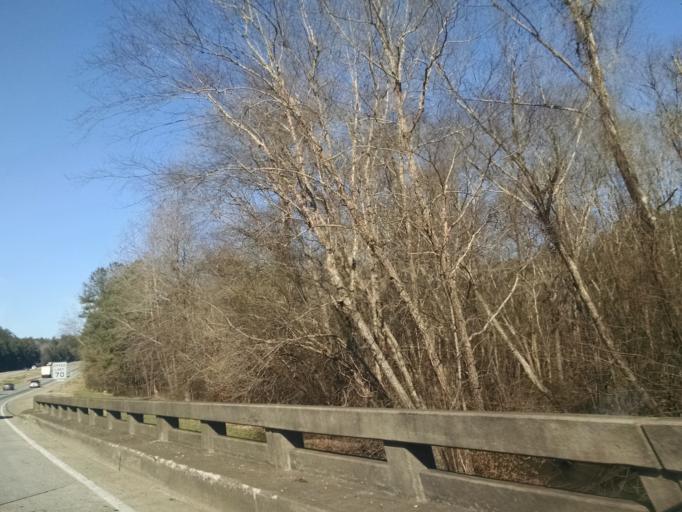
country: US
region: Georgia
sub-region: Gwinnett County
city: Suwanee
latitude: 34.0476
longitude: -84.0287
